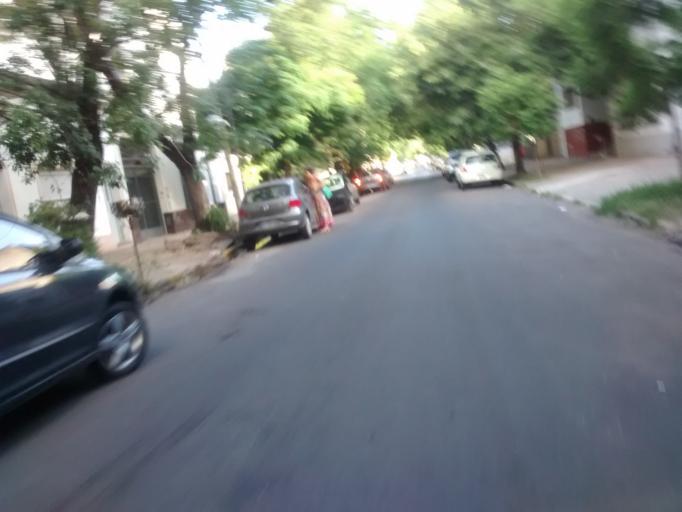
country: AR
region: Buenos Aires
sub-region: Partido de La Plata
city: La Plata
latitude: -34.9281
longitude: -57.9525
